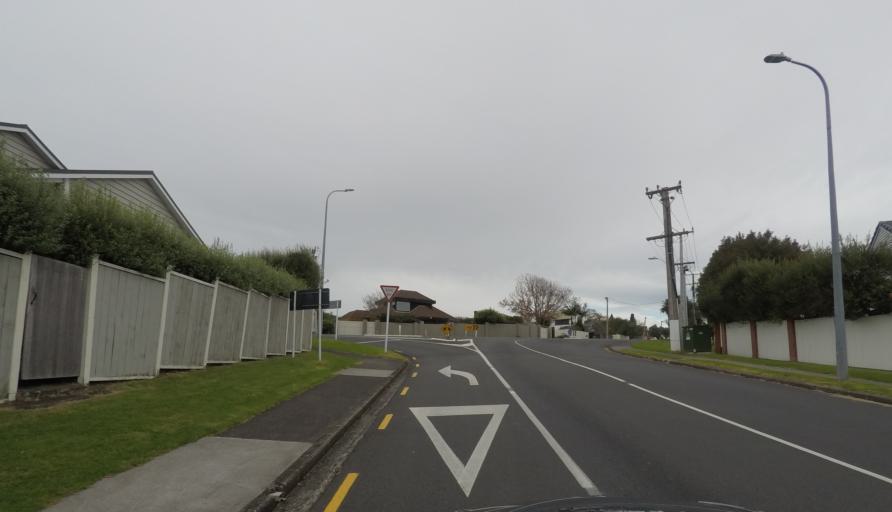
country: NZ
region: Auckland
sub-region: Auckland
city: Pakuranga
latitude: -36.8966
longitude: 174.9442
